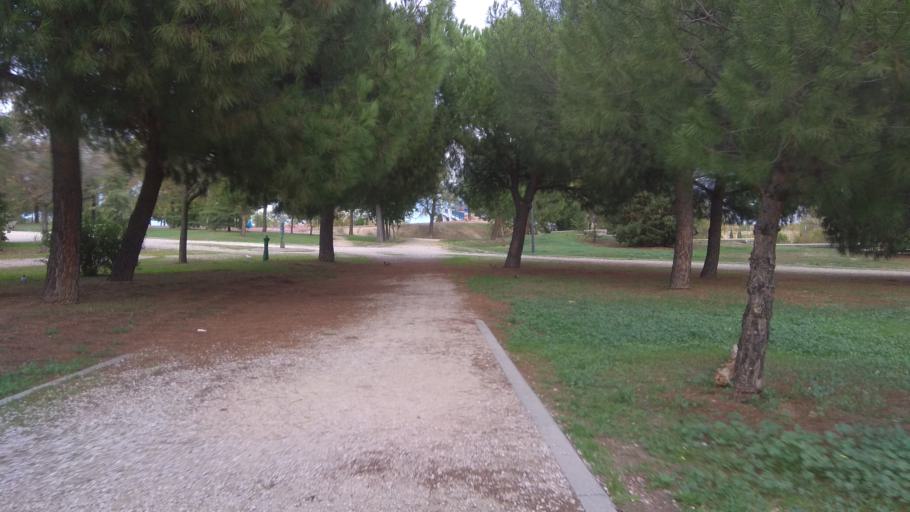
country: ES
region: Madrid
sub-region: Provincia de Madrid
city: Vicalvaro
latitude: 40.4112
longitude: -3.6162
